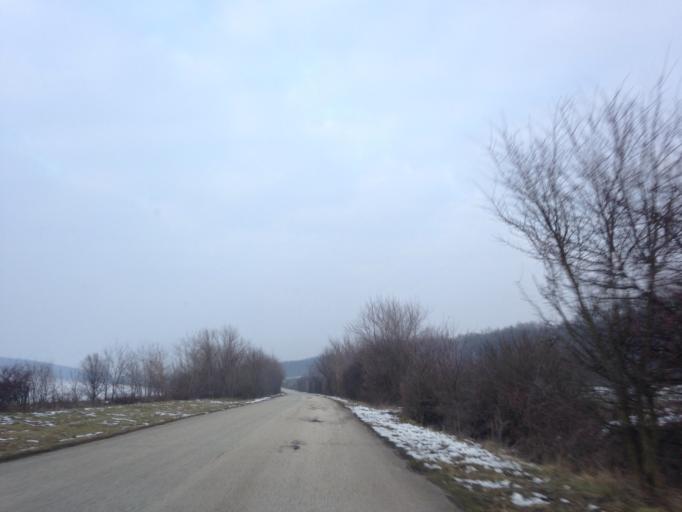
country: SK
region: Nitriansky
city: Surany
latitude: 48.0558
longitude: 18.3714
